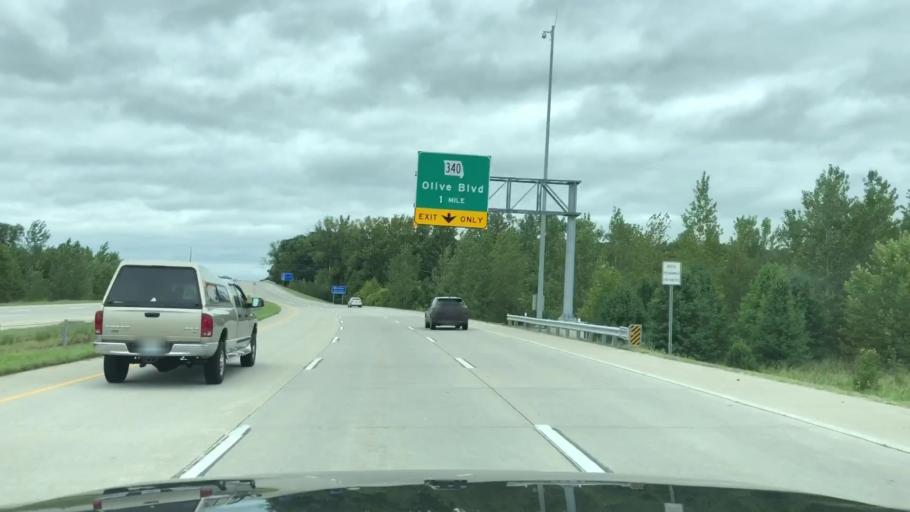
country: US
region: Missouri
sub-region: Saint Louis County
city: Maryland Heights
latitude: 38.6965
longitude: -90.5026
